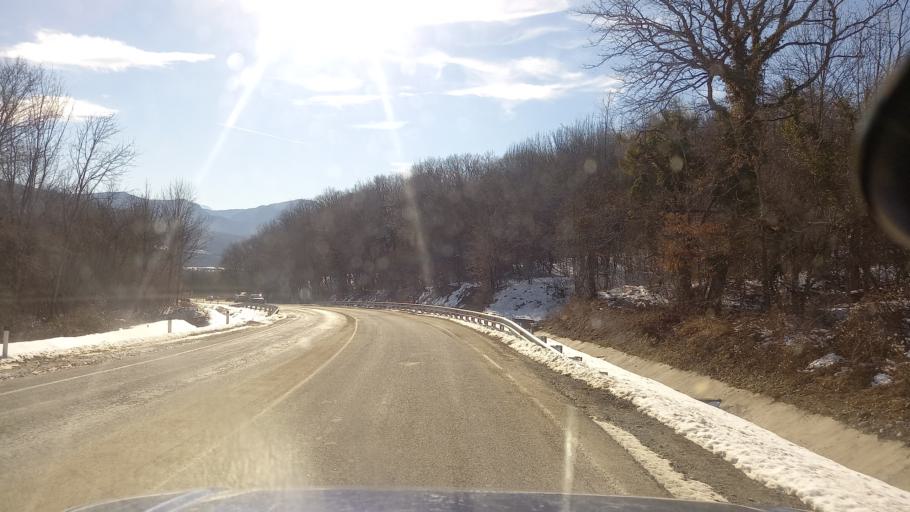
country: RU
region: Adygeya
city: Kamennomostskiy
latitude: 44.2452
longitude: 40.1909
